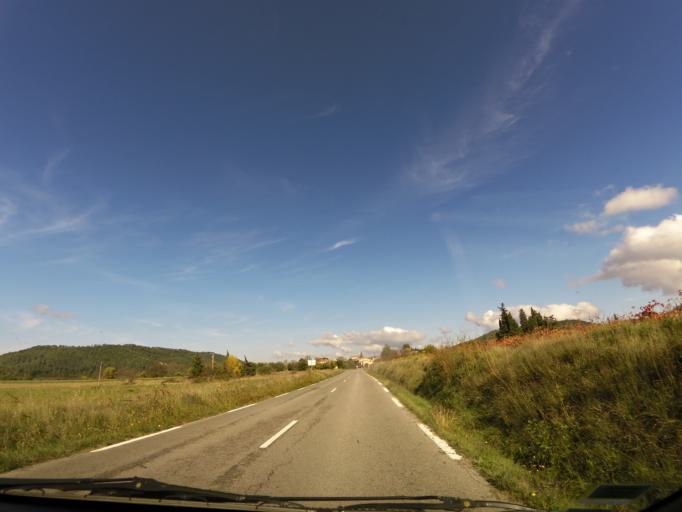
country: FR
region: Languedoc-Roussillon
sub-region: Departement du Gard
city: Saint-Mamert-du-Gard
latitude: 43.8946
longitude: 4.1006
